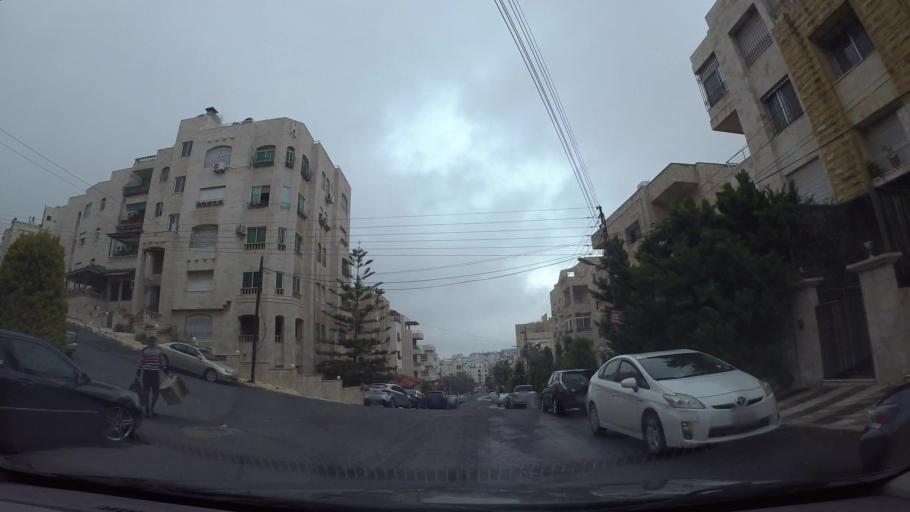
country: JO
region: Amman
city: Wadi as Sir
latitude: 31.9392
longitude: 35.8642
